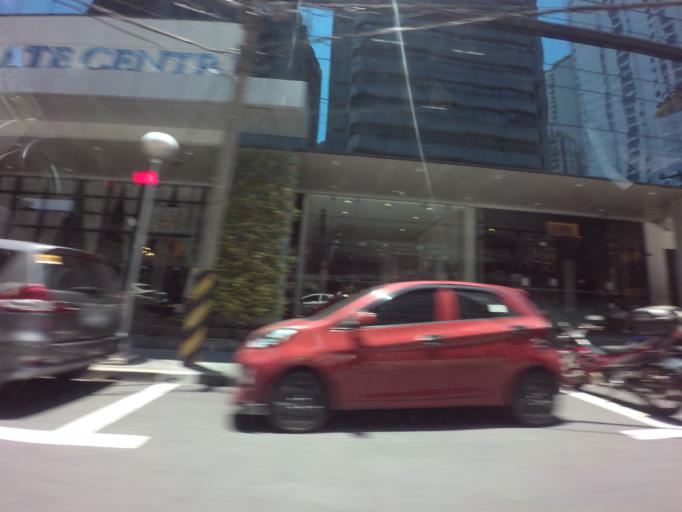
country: PH
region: Metro Manila
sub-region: Makati City
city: Makati City
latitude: 14.5604
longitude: 121.0246
